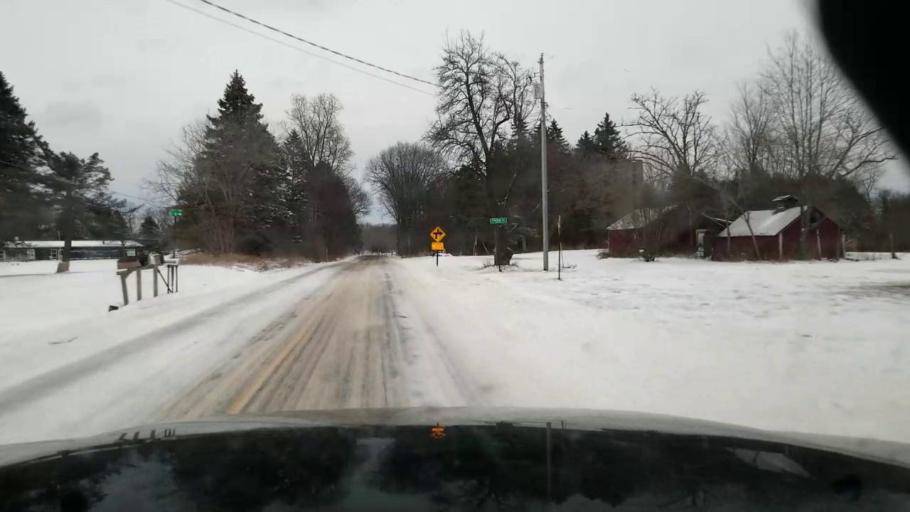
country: US
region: Michigan
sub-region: Jackson County
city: Vandercook Lake
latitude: 42.0946
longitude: -84.4688
